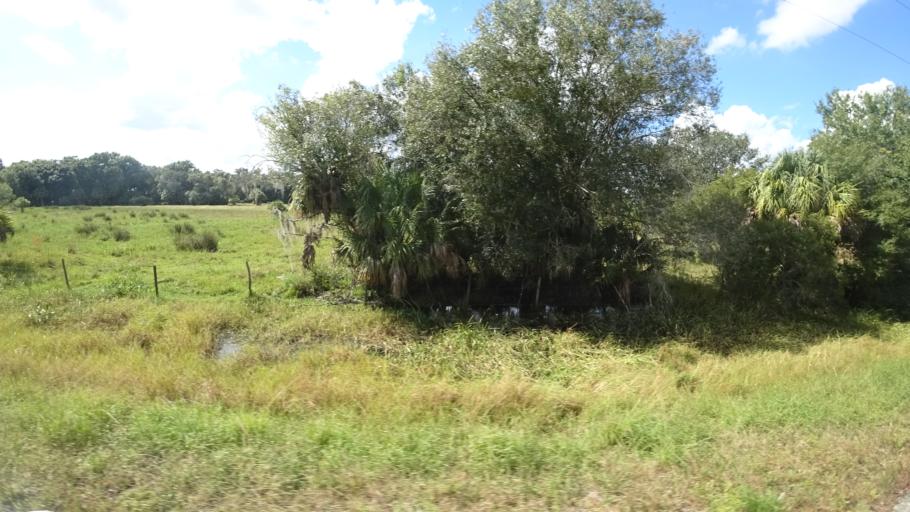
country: US
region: Florida
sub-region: Sarasota County
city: North Port
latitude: 27.2118
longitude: -82.1221
